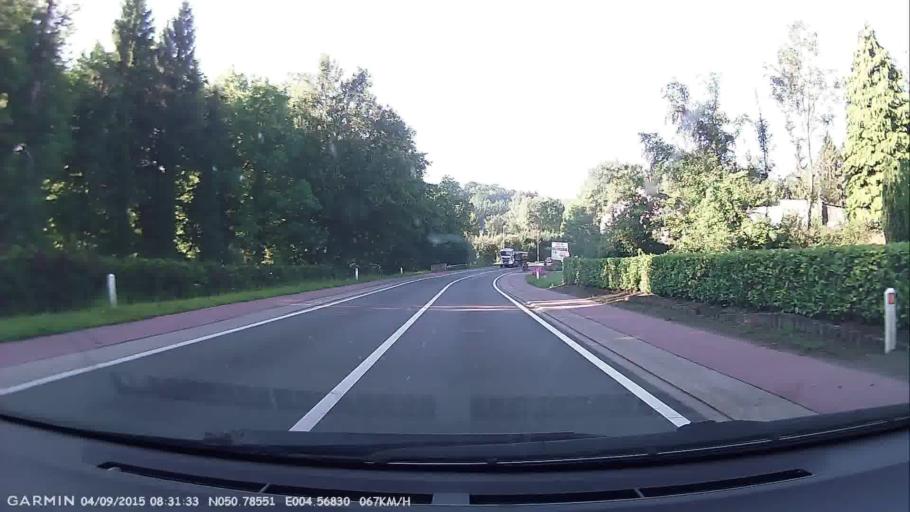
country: BE
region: Flanders
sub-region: Provincie Vlaams-Brabant
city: Huldenberg
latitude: 50.7852
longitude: 4.5680
